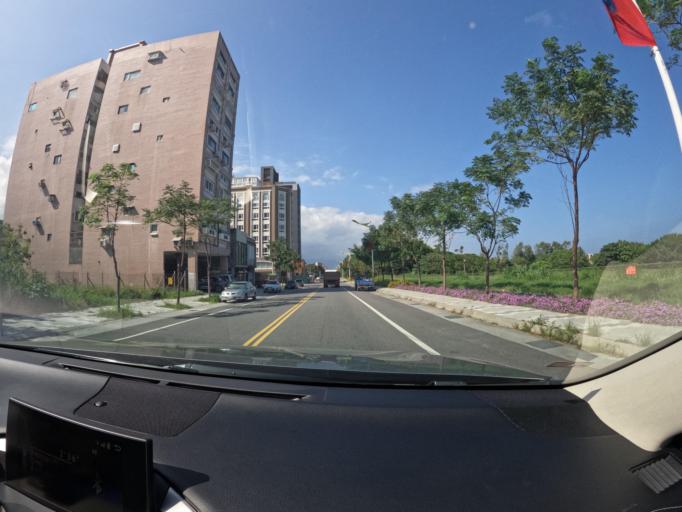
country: TW
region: Taiwan
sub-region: Hualien
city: Hualian
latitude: 23.9933
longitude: 121.6337
